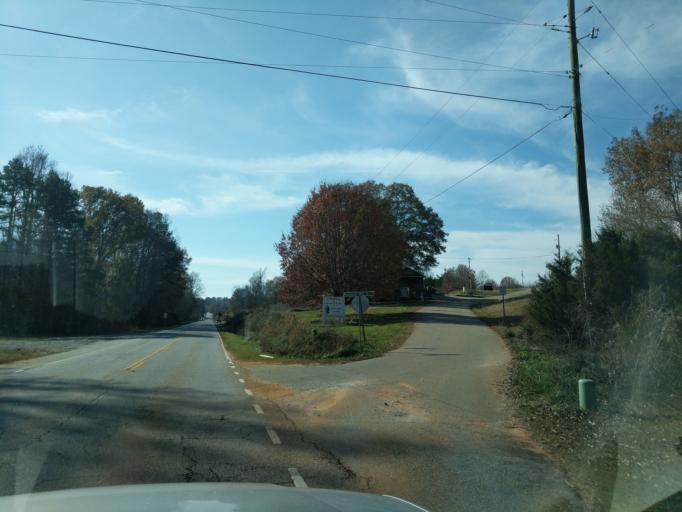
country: US
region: South Carolina
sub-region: Pickens County
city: Pickens
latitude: 34.8680
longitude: -82.7586
